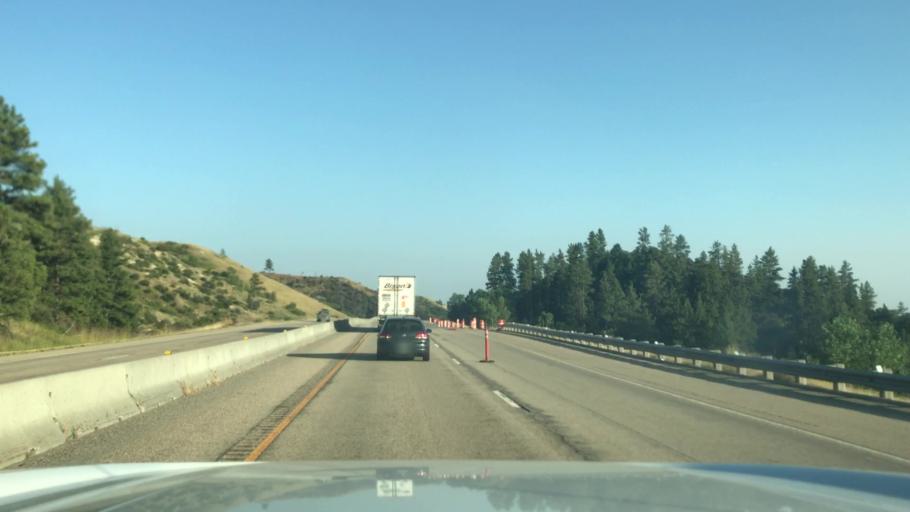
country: US
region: Montana
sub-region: Big Horn County
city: Crow Agency
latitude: 45.3377
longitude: -107.3510
